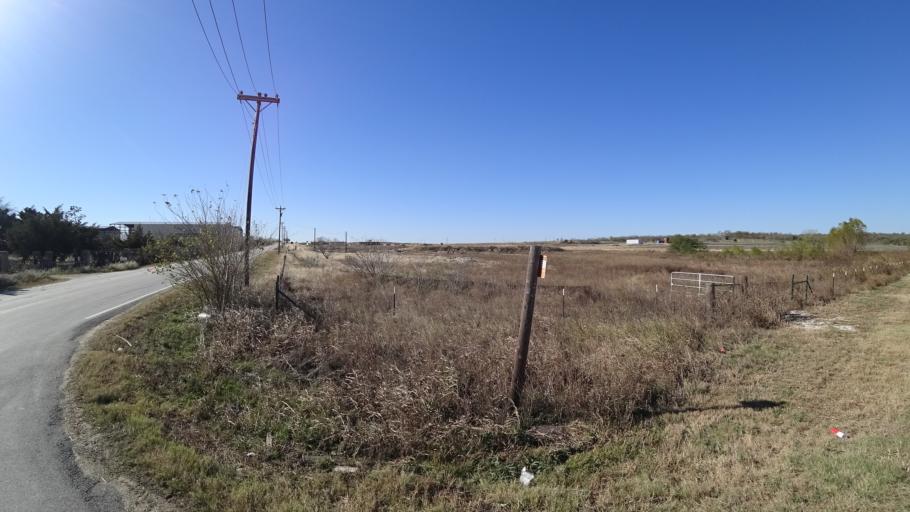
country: US
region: Texas
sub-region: Travis County
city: Onion Creek
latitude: 30.1218
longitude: -97.6678
